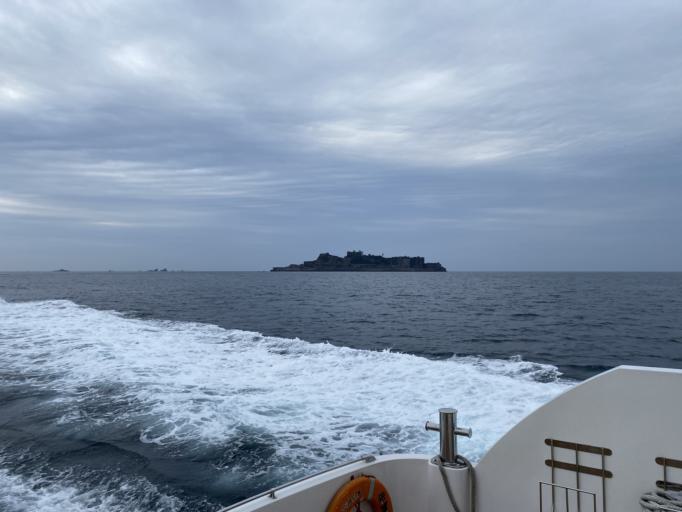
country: JP
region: Nagasaki
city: Nagasaki-shi
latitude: 32.6267
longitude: 129.7520
